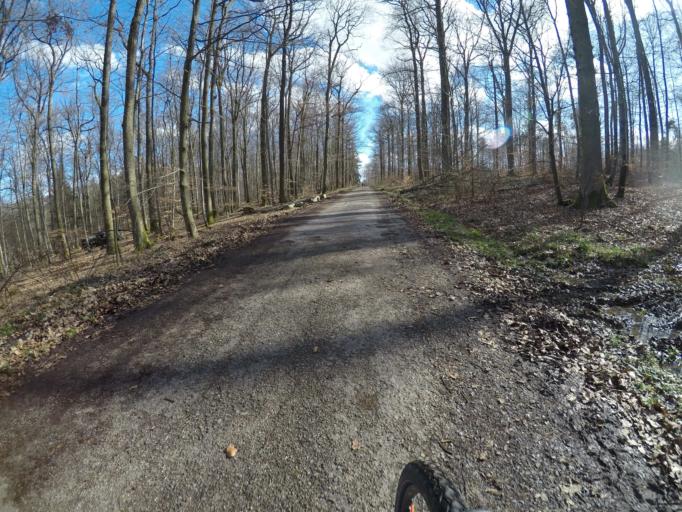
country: DE
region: Baden-Wuerttemberg
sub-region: Regierungsbezirk Stuttgart
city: Leinfelden-Echterdingen
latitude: 48.6835
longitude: 9.1437
